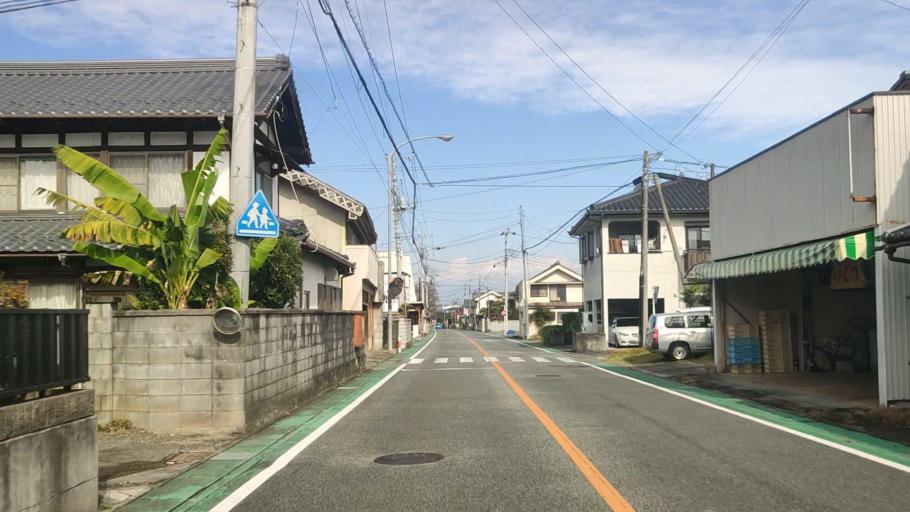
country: JP
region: Yamanashi
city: Ryuo
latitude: 35.5673
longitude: 138.4648
